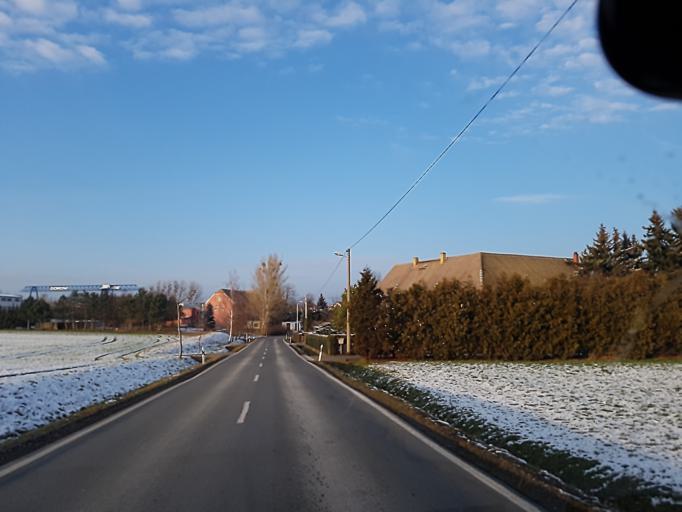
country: DE
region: Saxony
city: Oschatz
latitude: 51.2857
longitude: 13.1366
